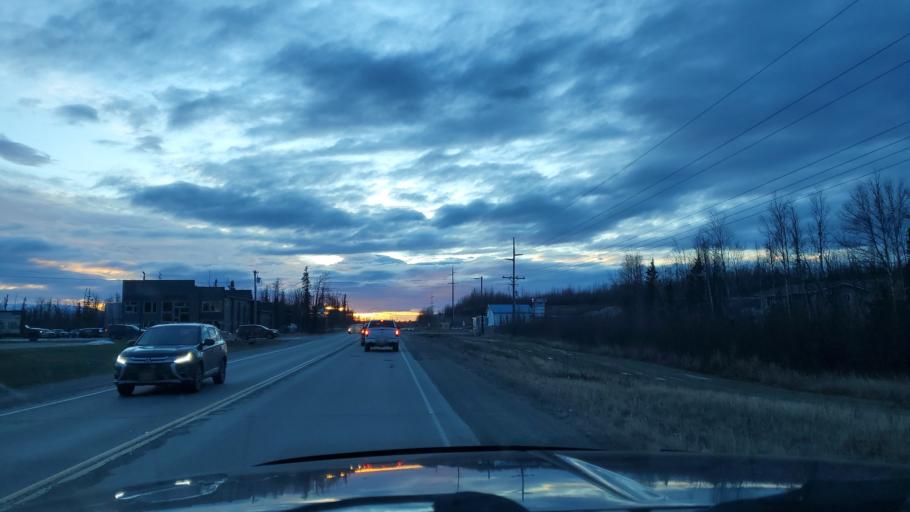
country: US
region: Alaska
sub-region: Matanuska-Susitna Borough
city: Lakes
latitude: 61.6031
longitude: -149.3537
